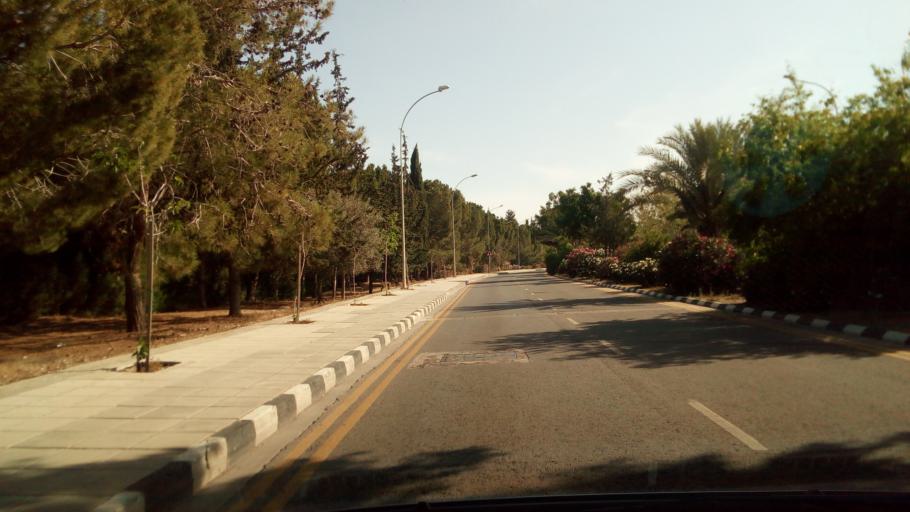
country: CY
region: Pafos
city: Paphos
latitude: 34.7581
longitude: 32.4333
